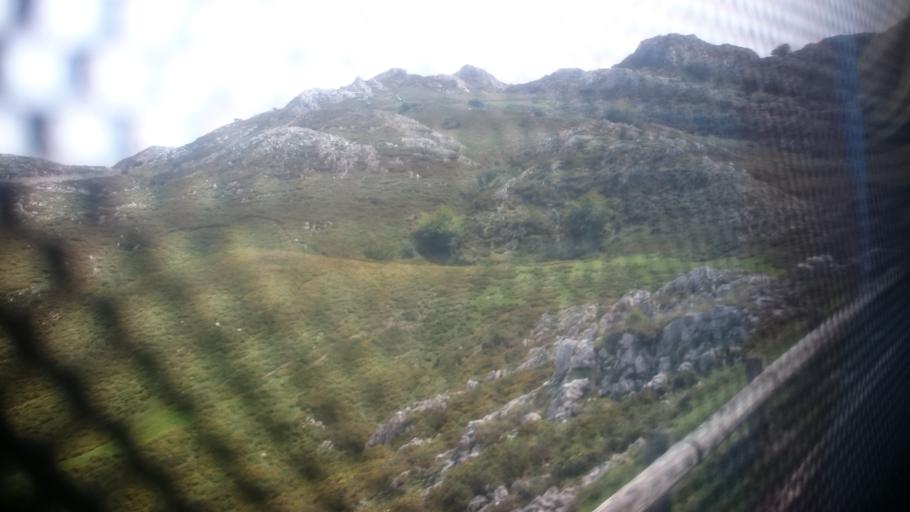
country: ES
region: Asturias
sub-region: Province of Asturias
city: Amieva
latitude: 43.2907
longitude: -5.0097
